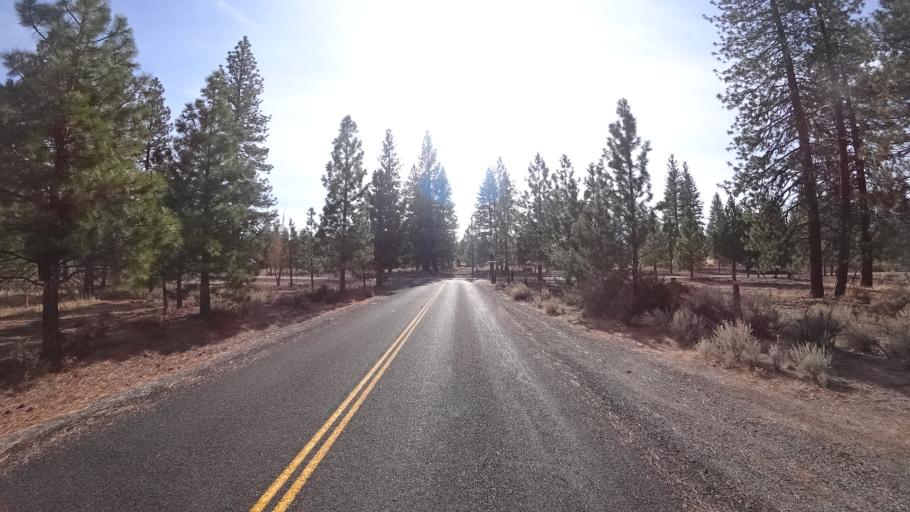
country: US
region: California
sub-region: Siskiyou County
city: Weed
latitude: 41.4945
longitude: -122.3809
